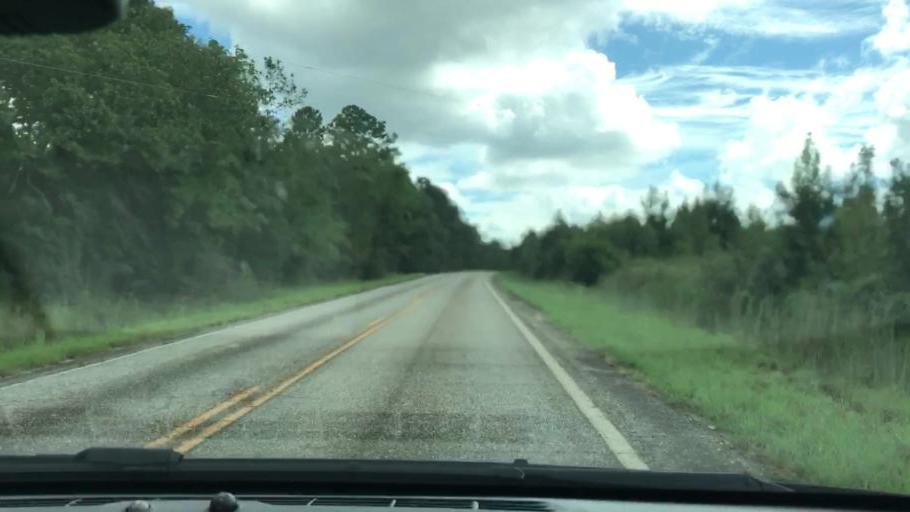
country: US
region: Georgia
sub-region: Stewart County
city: Lumpkin
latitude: 32.0715
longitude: -84.8471
